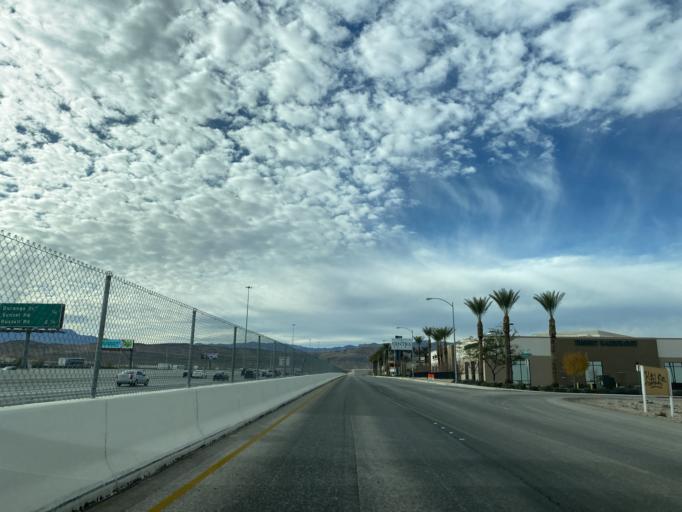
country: US
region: Nevada
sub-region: Clark County
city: Spring Valley
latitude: 36.0667
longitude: -115.2695
